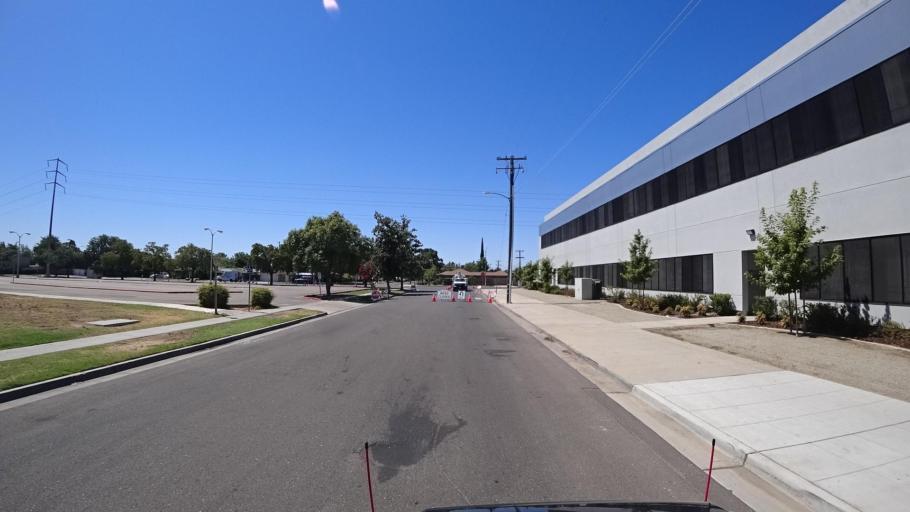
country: US
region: California
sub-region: Fresno County
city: Fresno
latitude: 36.7875
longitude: -119.7871
